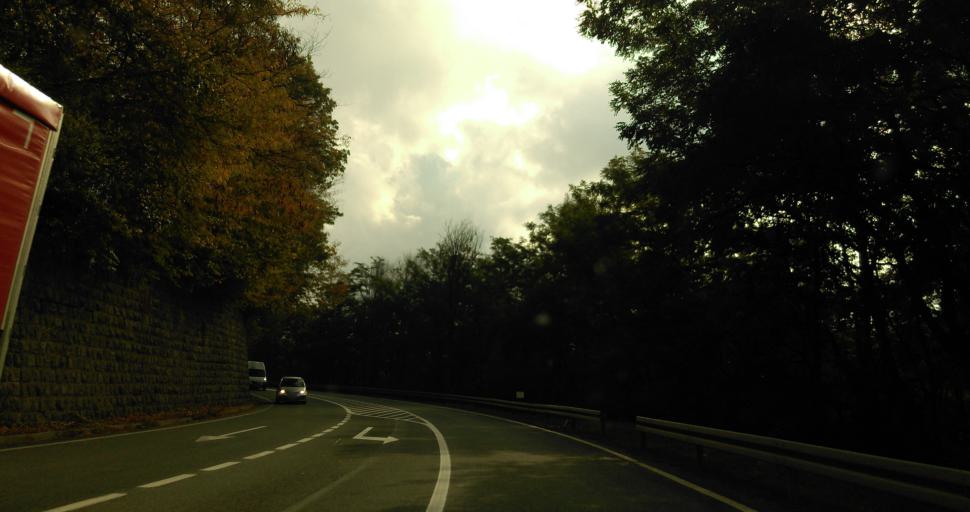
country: RS
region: Central Serbia
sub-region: Kolubarski Okrug
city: Ljig
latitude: 44.1961
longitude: 20.2874
